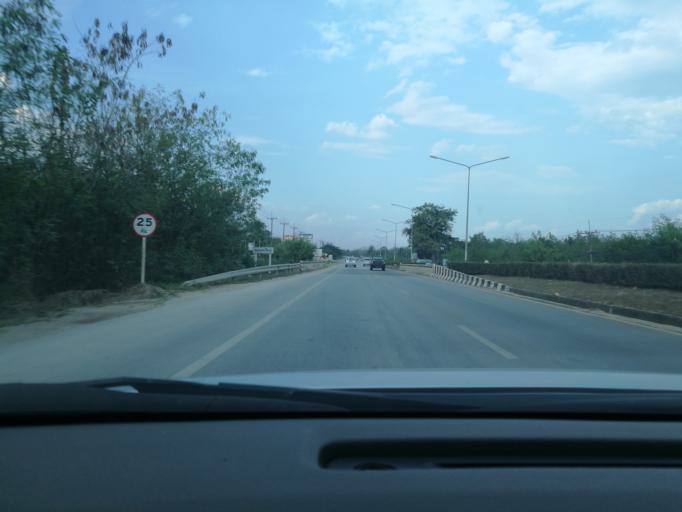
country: TH
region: Phetchabun
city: Phetchabun
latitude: 16.4668
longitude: 101.1575
